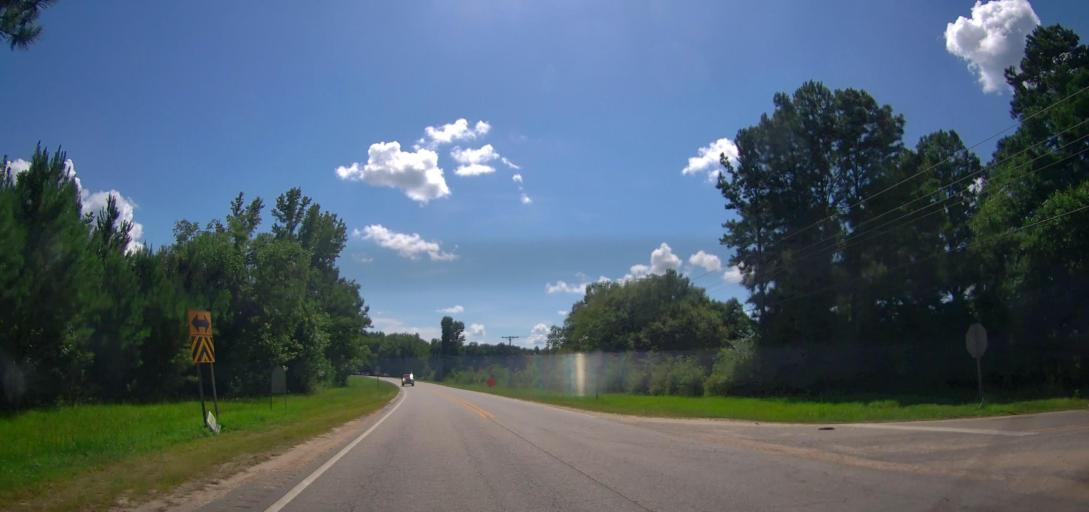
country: US
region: Alabama
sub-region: Macon County
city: Tuskegee
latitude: 32.3840
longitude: -85.8217
